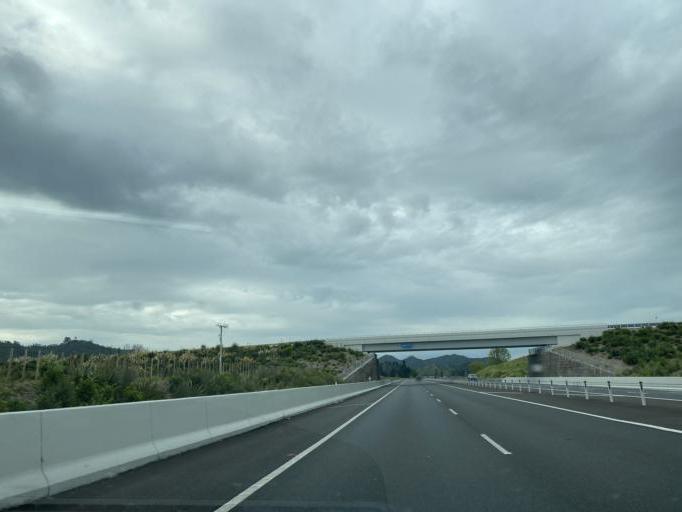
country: NZ
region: Waikato
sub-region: Waikato District
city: Ngaruawahia
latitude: -37.6132
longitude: 175.2047
